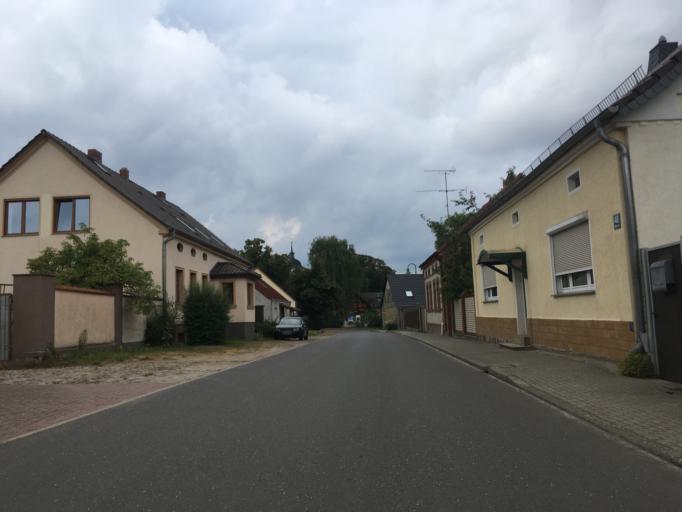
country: DE
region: Brandenburg
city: Angermunde
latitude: 52.9801
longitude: 13.9606
